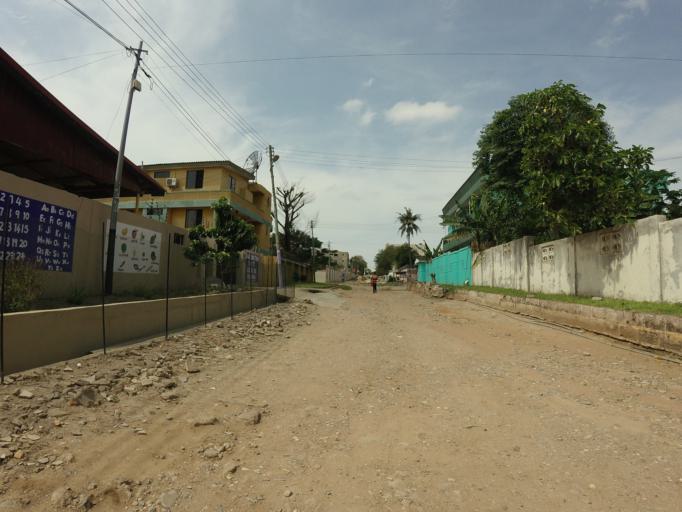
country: GH
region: Greater Accra
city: Dome
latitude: 5.6290
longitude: -0.2339
